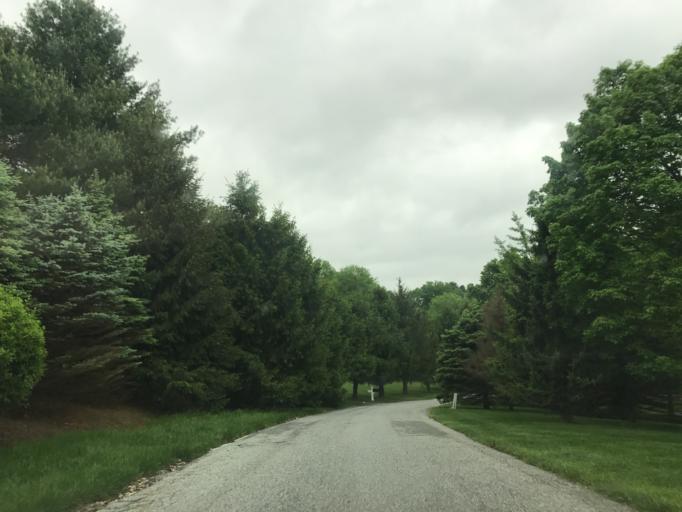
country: US
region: Maryland
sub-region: Baltimore County
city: Hunt Valley
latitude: 39.5164
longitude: -76.6246
